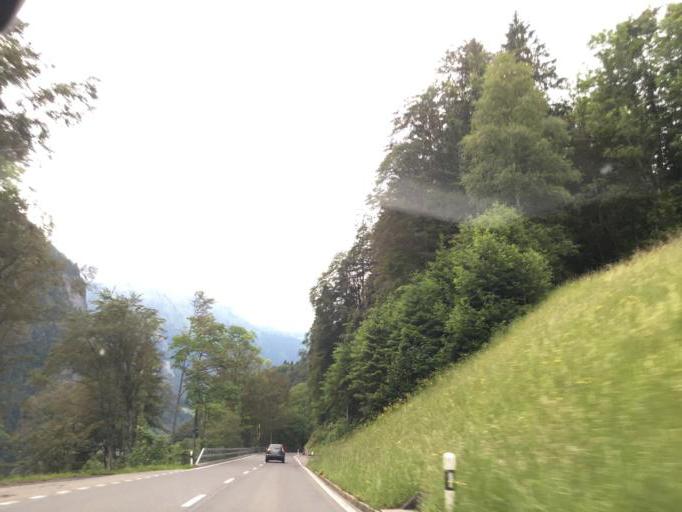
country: CH
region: Obwalden
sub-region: Obwalden
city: Engelberg
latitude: 46.8287
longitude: 8.3782
